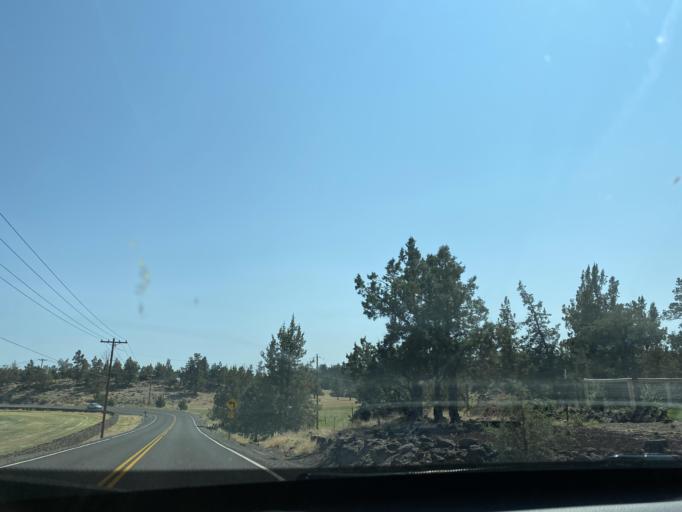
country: US
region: Oregon
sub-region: Deschutes County
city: Terrebonne
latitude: 44.3690
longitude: -121.1636
